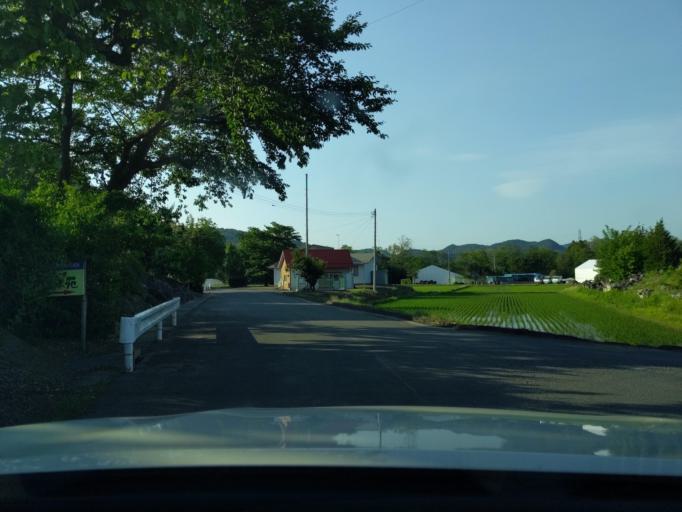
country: JP
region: Fukushima
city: Motomiya
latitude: 37.4707
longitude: 140.3302
